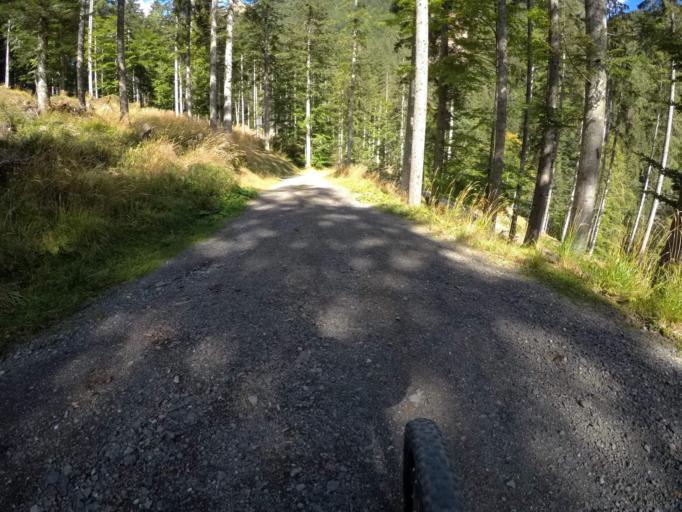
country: IT
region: Friuli Venezia Giulia
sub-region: Provincia di Udine
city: Ligosullo
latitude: 46.5829
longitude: 13.0860
